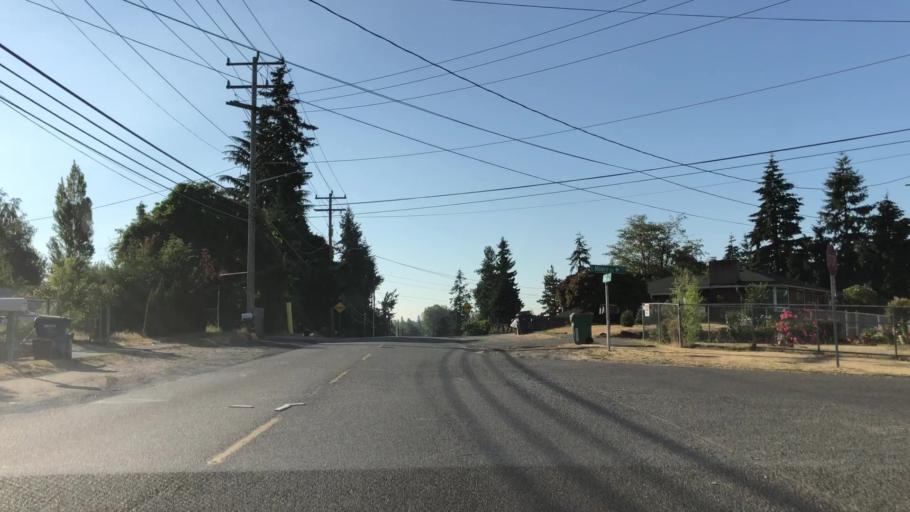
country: US
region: Washington
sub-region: King County
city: Bryn Mawr-Skyway
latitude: 47.4994
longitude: -122.2657
